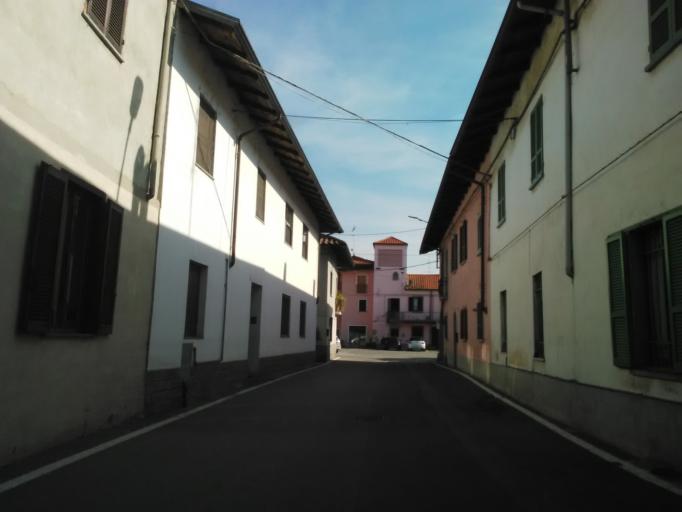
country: IT
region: Piedmont
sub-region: Provincia di Vercelli
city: Lenta
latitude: 45.5545
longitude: 8.3847
